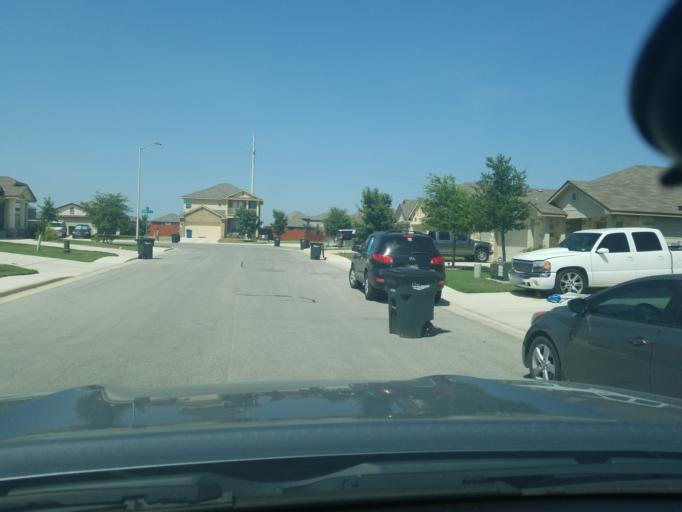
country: US
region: Texas
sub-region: Guadalupe County
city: Lake Dunlap
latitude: 29.6693
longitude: -98.0371
